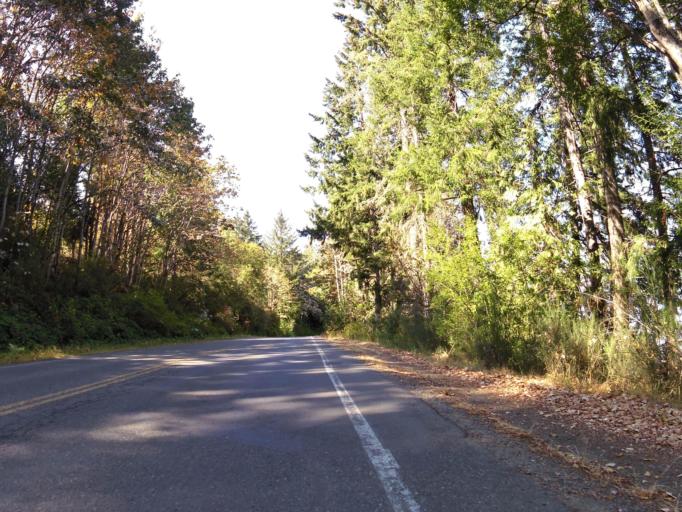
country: CA
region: British Columbia
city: North Saanich
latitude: 48.6252
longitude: -123.5272
